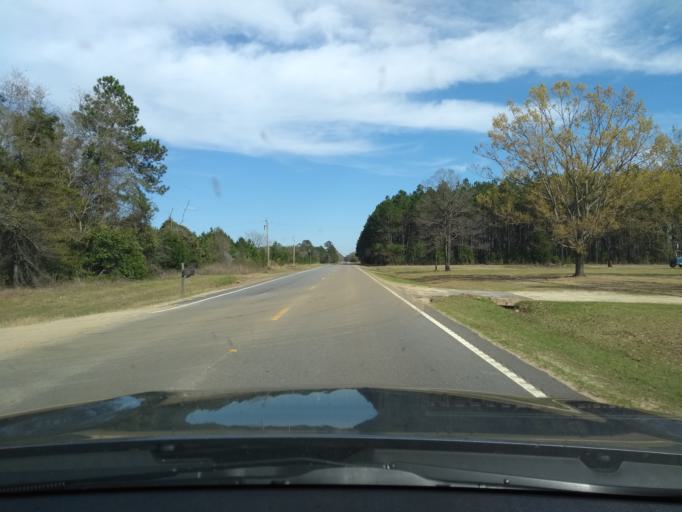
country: US
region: Georgia
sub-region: Bulloch County
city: Brooklet
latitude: 32.4808
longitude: -81.5945
